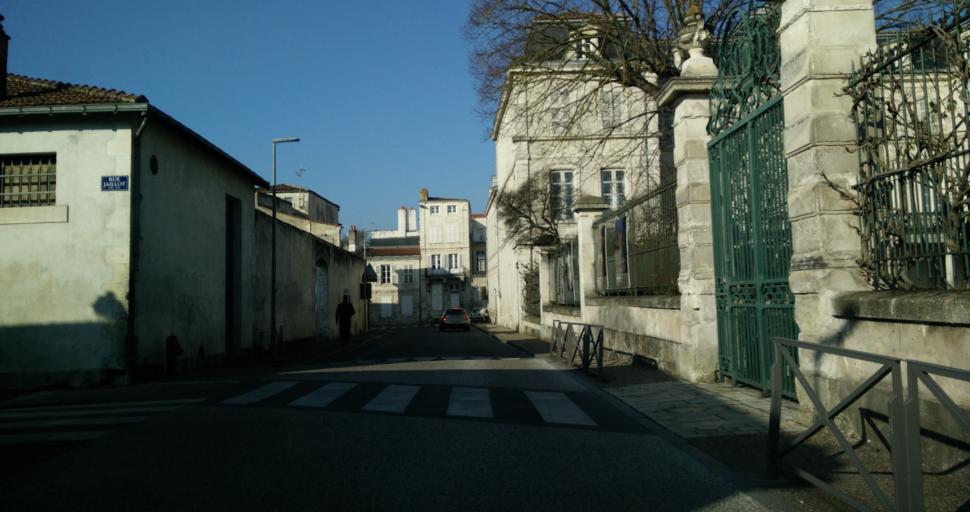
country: FR
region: Poitou-Charentes
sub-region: Departement de la Charente-Maritime
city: La Rochelle
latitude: 46.1646
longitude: -1.1506
